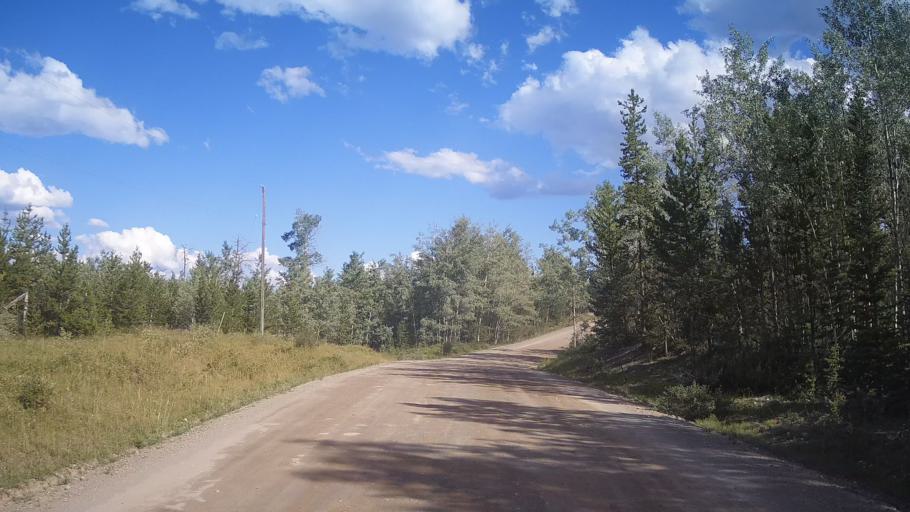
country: CA
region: British Columbia
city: Cache Creek
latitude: 51.2756
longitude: -121.7294
